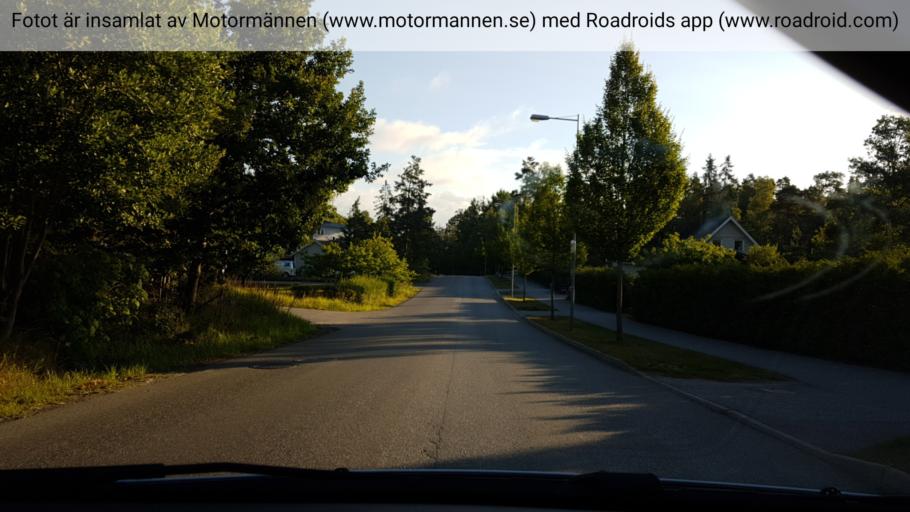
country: SE
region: Stockholm
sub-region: Nacka Kommun
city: Fisksatra
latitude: 59.2493
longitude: 18.2745
